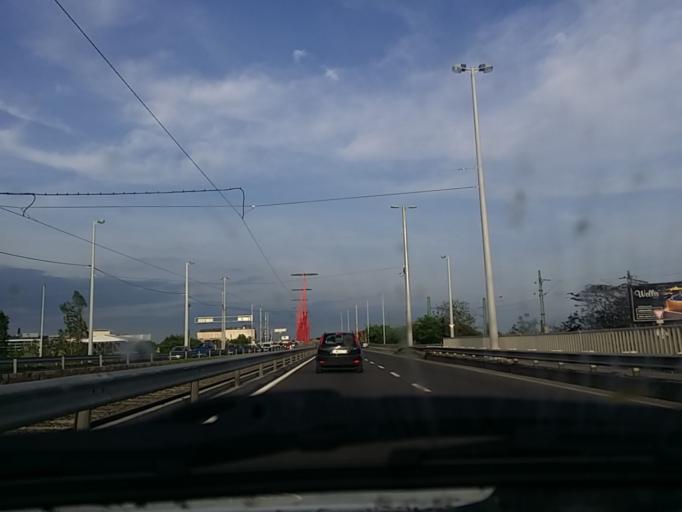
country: HU
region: Budapest
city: Budapest IX. keruelet
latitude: 47.4690
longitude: 19.0603
